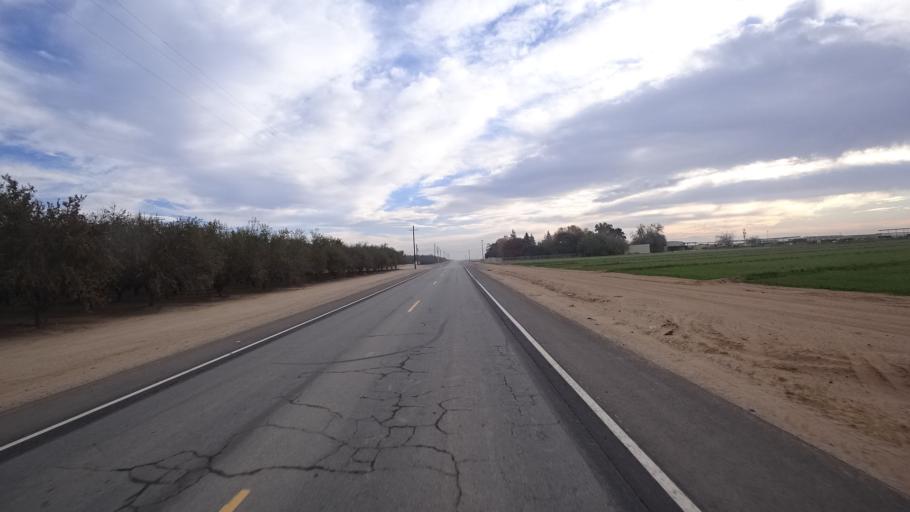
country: US
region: California
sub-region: Kern County
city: Rosedale
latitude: 35.4197
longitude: -119.2054
